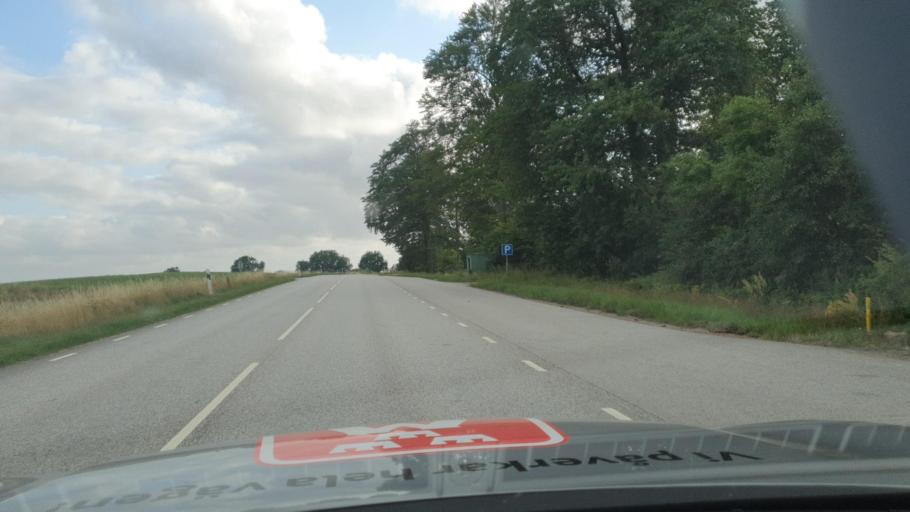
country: SE
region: Skane
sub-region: Eslovs Kommun
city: Stehag
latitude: 55.9134
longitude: 13.3605
